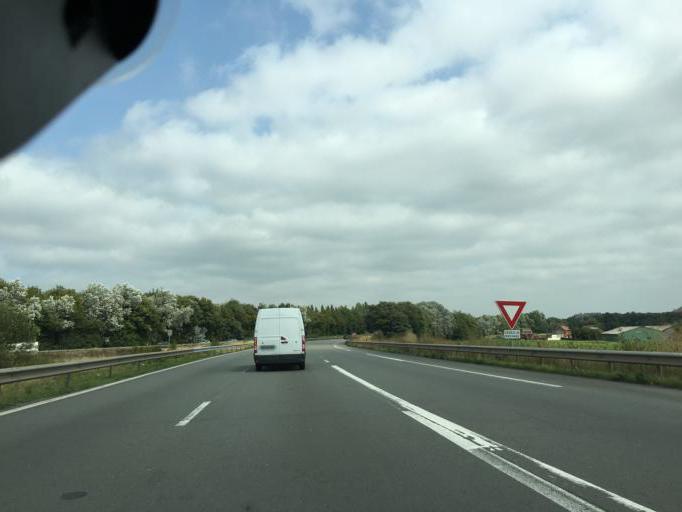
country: FR
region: Nord-Pas-de-Calais
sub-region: Departement du Pas-de-Calais
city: Noyelles-Godault
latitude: 50.4263
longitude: 2.9883
